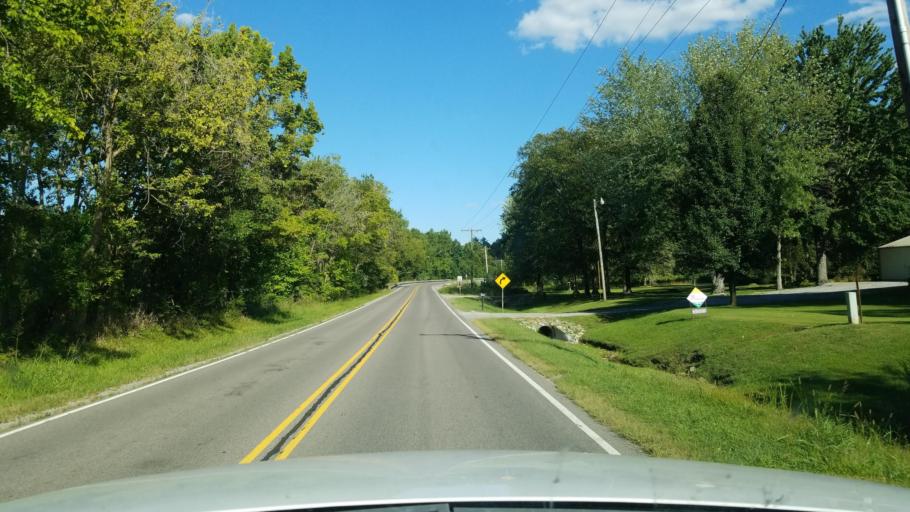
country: US
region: Illinois
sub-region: Saline County
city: Harrisburg
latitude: 37.6364
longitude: -88.4882
